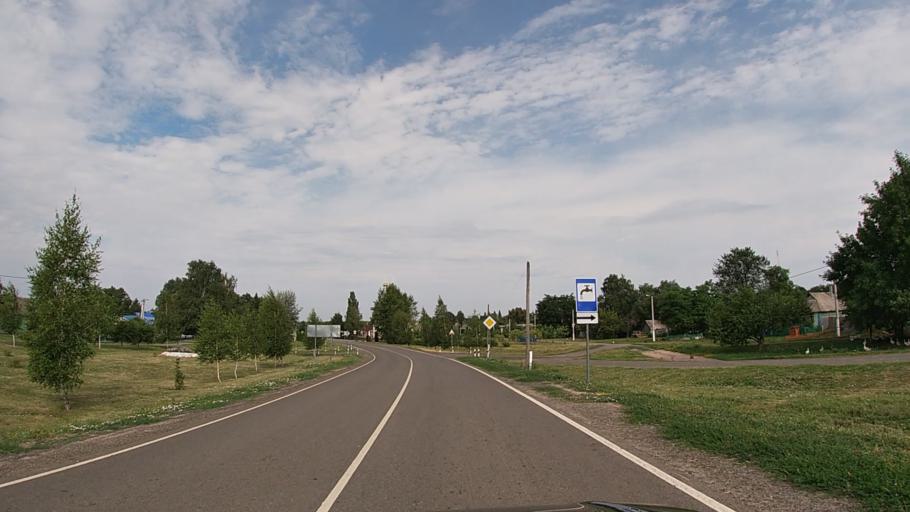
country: UA
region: Sumy
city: Krasnopillya
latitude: 50.8140
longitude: 35.4436
